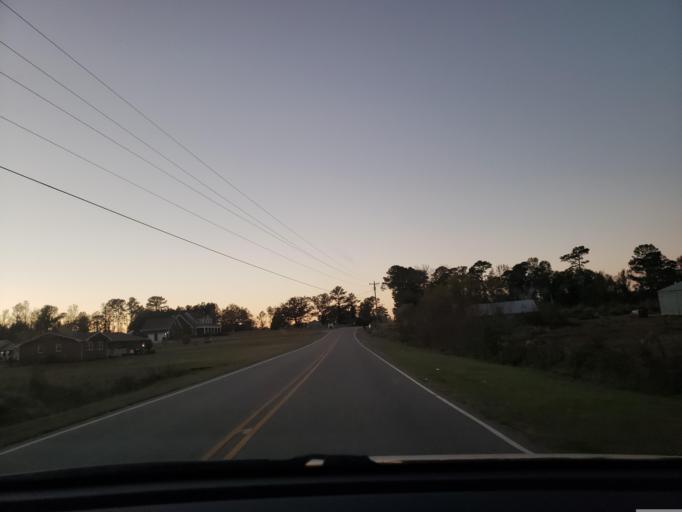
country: US
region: North Carolina
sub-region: Duplin County
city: Beulaville
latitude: 34.8032
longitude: -77.7836
